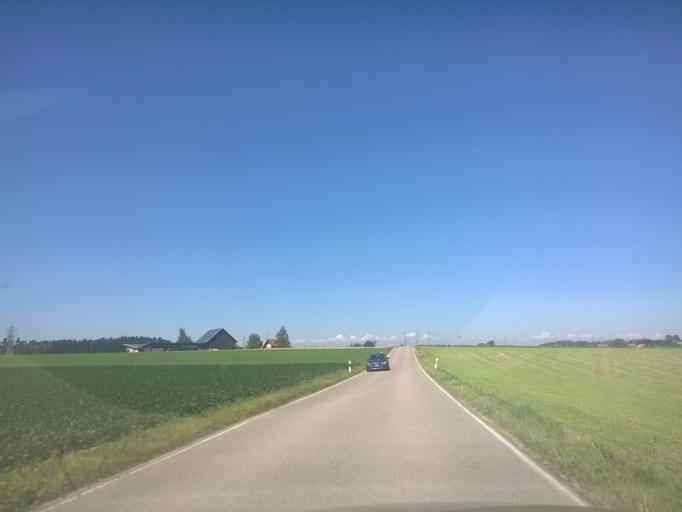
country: CH
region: Zurich
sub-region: Bezirk Winterthur
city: Brutten
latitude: 47.4792
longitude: 8.6637
